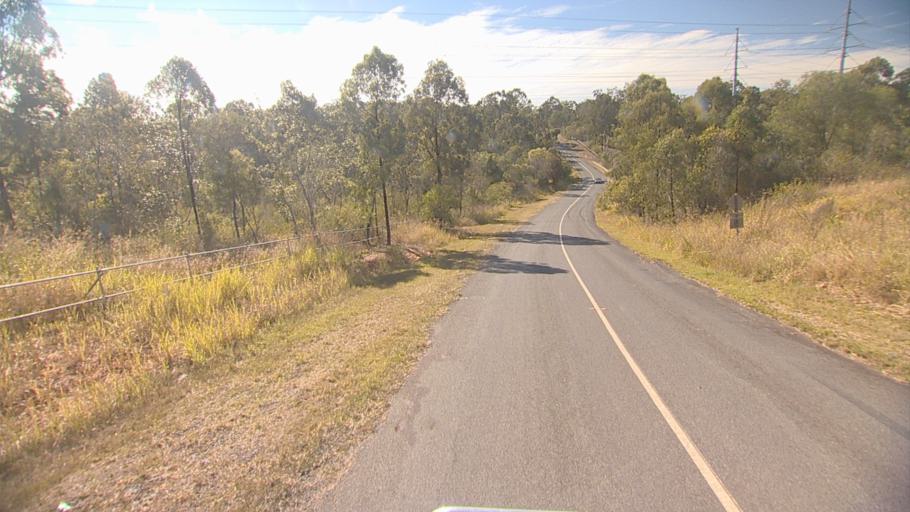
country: AU
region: Queensland
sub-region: Ipswich
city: Springfield Lakes
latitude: -27.7129
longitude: 152.9182
